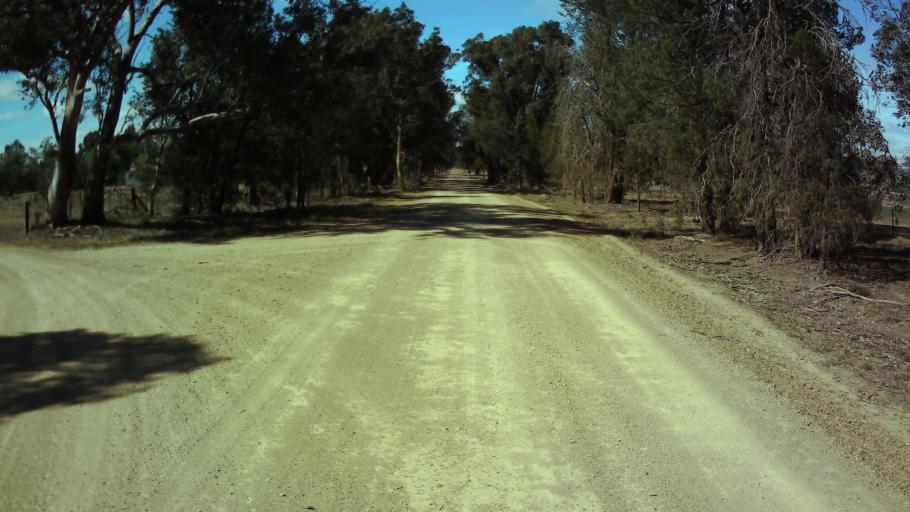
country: AU
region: New South Wales
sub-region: Weddin
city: Grenfell
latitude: -34.0420
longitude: 148.3155
